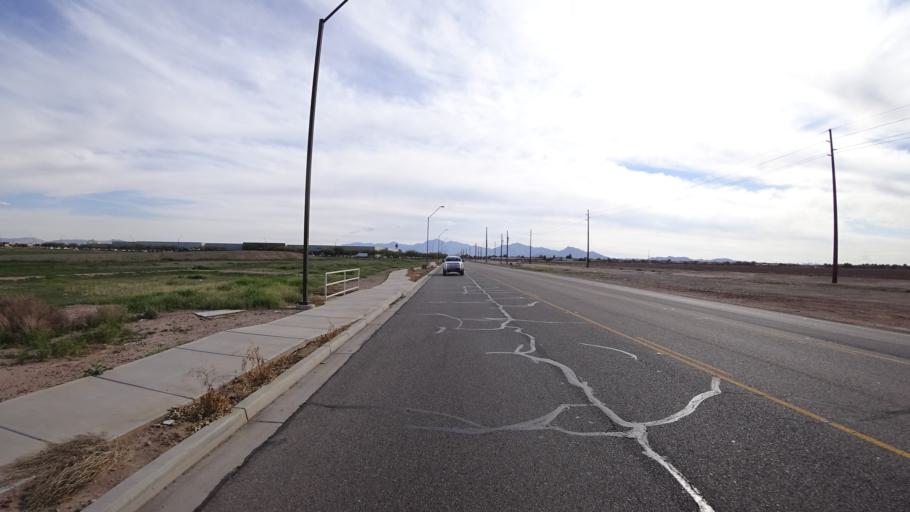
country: US
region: Arizona
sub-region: Maricopa County
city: Tolleson
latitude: 33.4556
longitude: -112.2898
